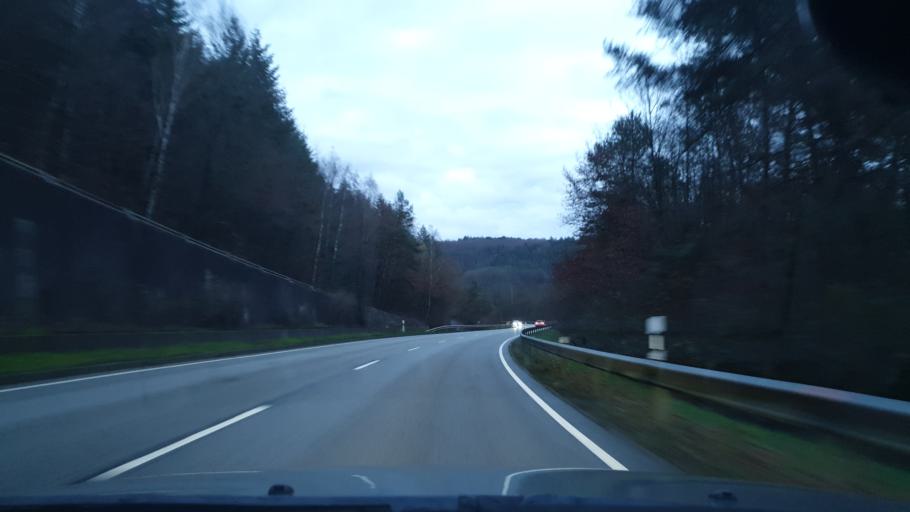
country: DE
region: Rheinland-Pfalz
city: Waldfischbach-Burgalben
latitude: 49.2948
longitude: 7.6589
